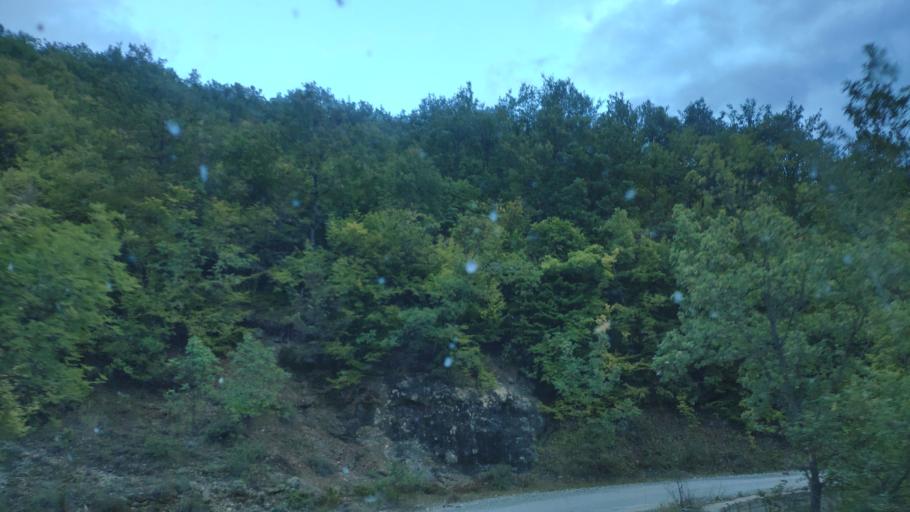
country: AL
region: Korce
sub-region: Rrethi i Kolonjes
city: Erseke
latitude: 40.2515
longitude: 20.8670
